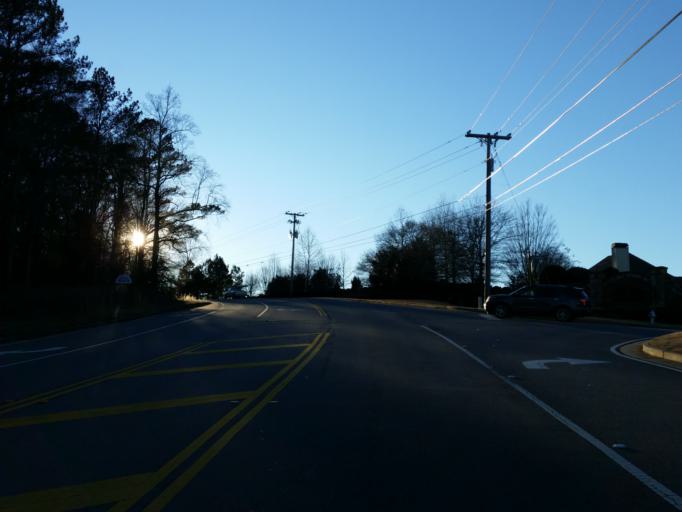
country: US
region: Georgia
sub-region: Cherokee County
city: Holly Springs
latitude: 34.1552
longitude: -84.4358
